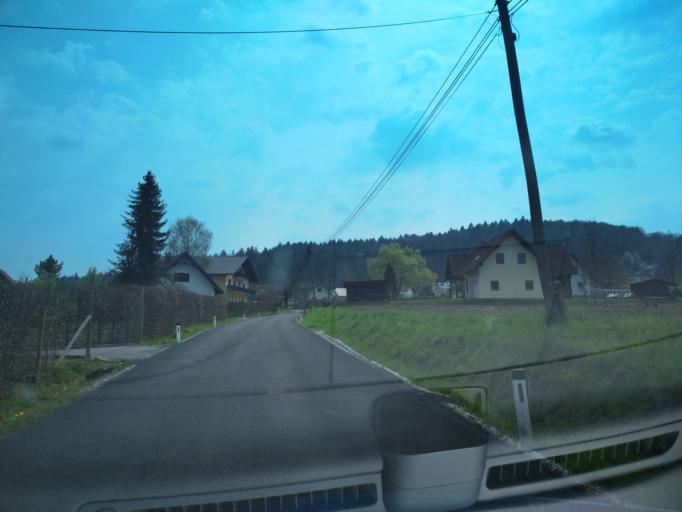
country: AT
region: Styria
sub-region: Politischer Bezirk Leibnitz
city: Kitzeck im Sausal
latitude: 46.7506
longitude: 15.4192
